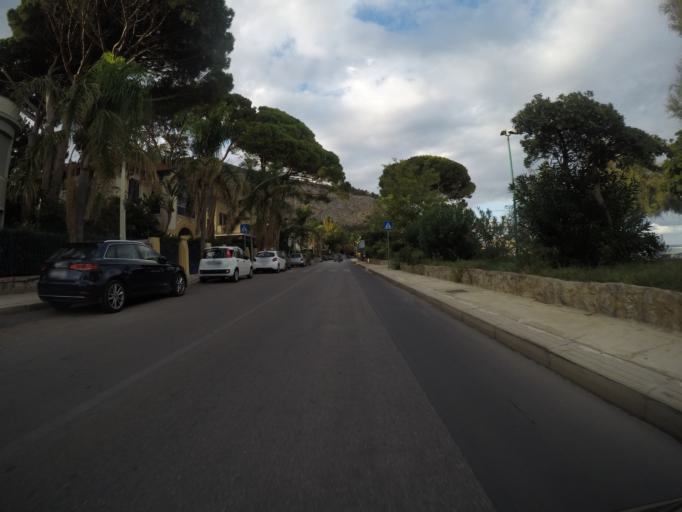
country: IT
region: Sicily
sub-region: Palermo
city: Palermo
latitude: 38.2046
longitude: 13.3251
